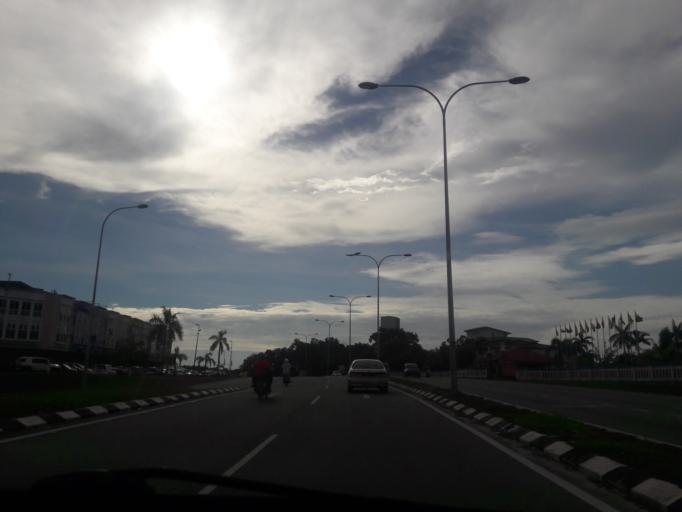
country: MY
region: Kedah
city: Sungai Petani
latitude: 5.6251
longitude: 100.5335
